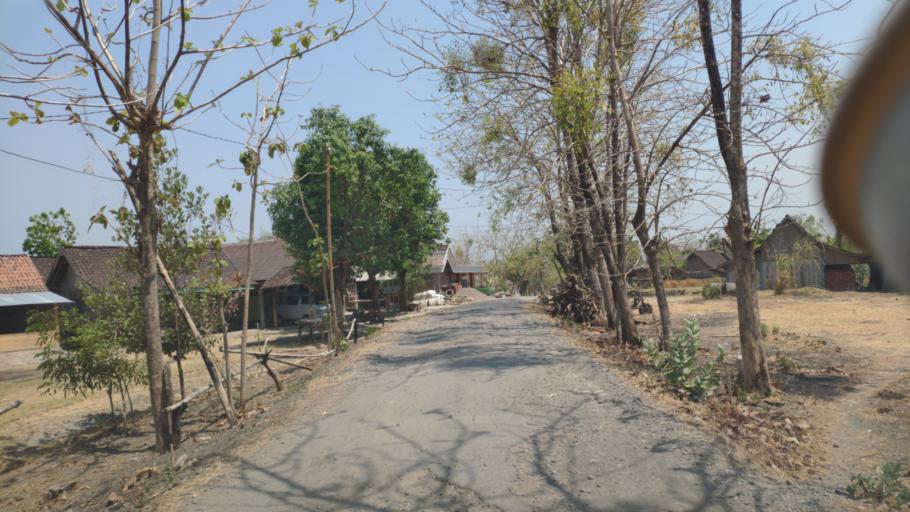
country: ID
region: West Java
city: Ngawi
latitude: -7.3338
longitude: 111.4252
